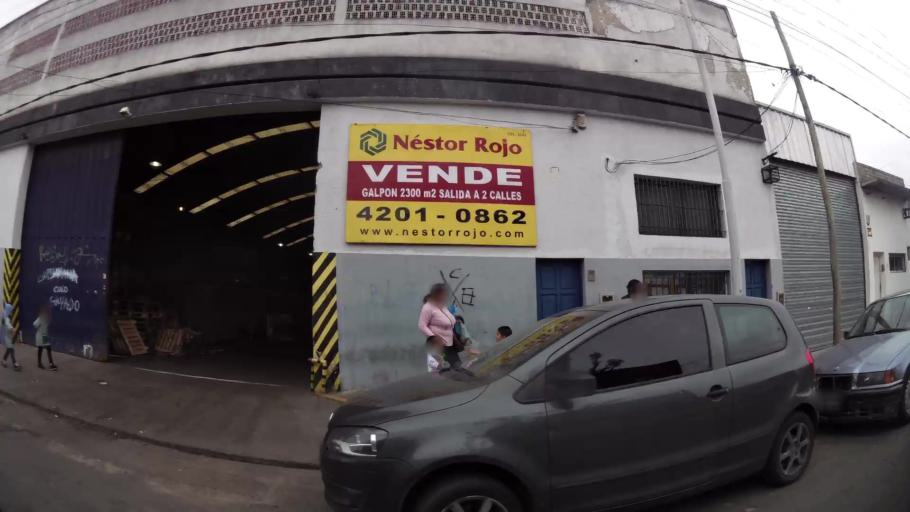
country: AR
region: Buenos Aires
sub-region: Partido de Avellaneda
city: Avellaneda
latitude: -34.6578
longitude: -58.3523
